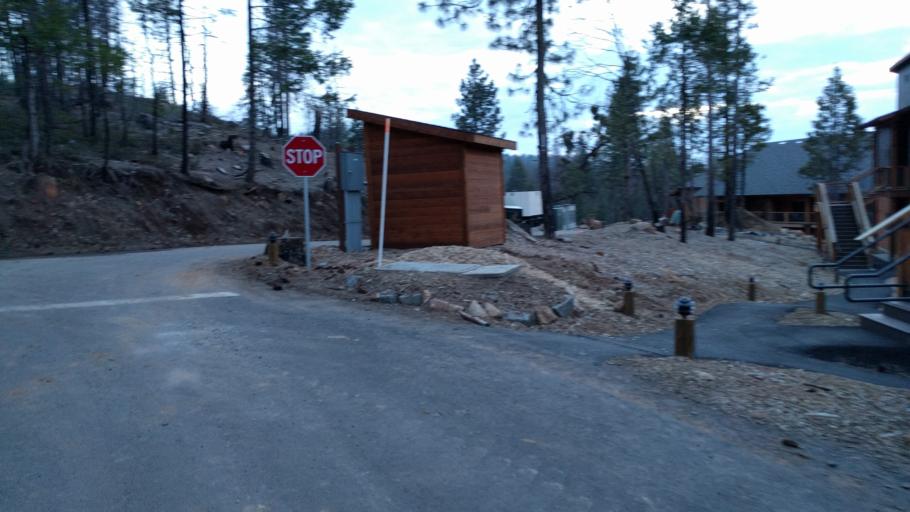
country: US
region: California
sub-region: Mariposa County
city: Midpines
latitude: 37.8122
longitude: -119.8804
